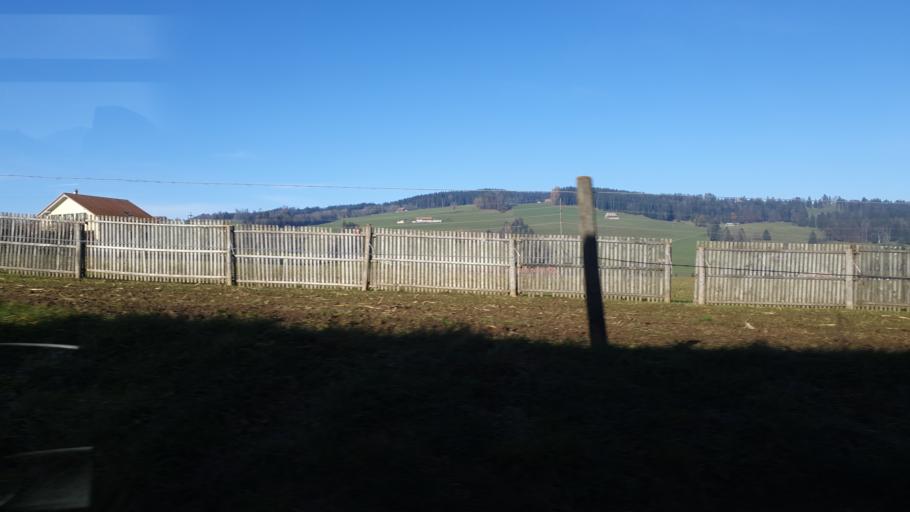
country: CH
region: Fribourg
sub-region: Gruyere District
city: Vuadens
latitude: 46.6201
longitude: 7.0243
